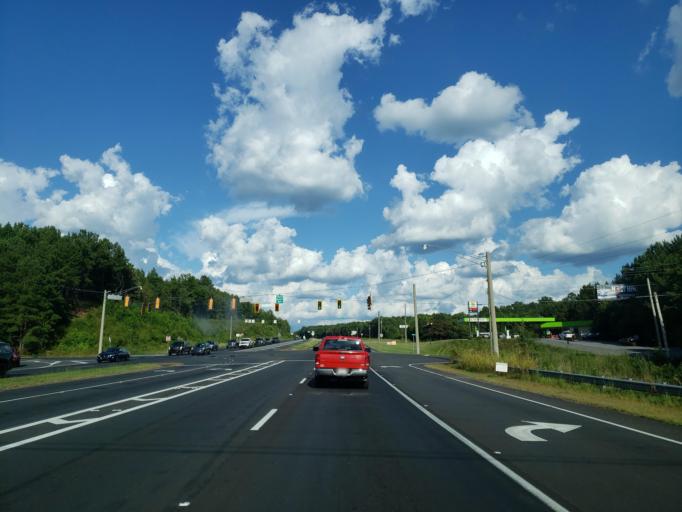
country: US
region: Georgia
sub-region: Floyd County
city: Rome
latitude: 34.2171
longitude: -85.1244
